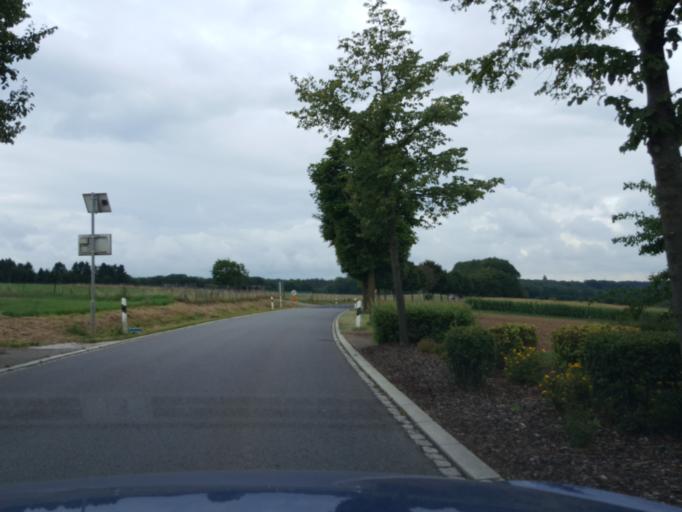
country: LU
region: Luxembourg
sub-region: Canton de Capellen
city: Kehlen
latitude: 49.6624
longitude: 6.0356
